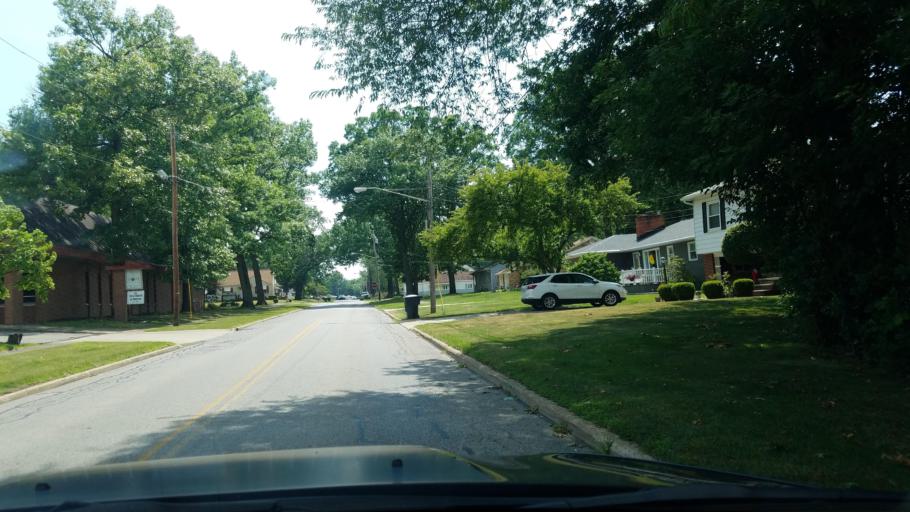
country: US
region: Ohio
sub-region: Trumbull County
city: Bolindale
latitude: 41.2249
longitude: -80.7785
